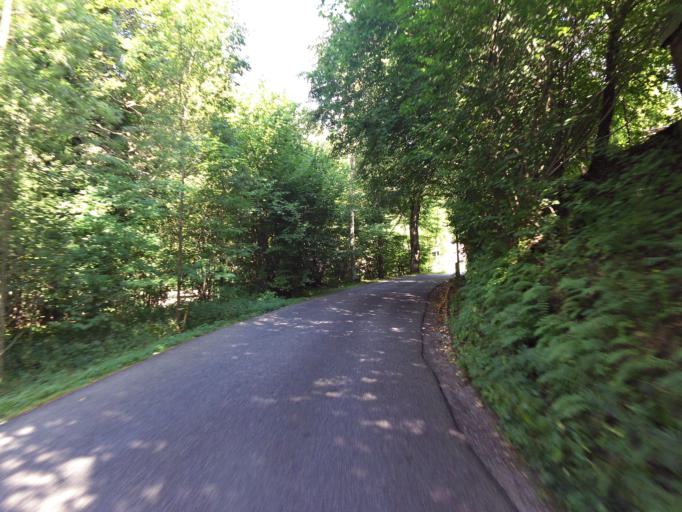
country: CZ
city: Cesky Dub
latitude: 50.6130
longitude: 14.9975
